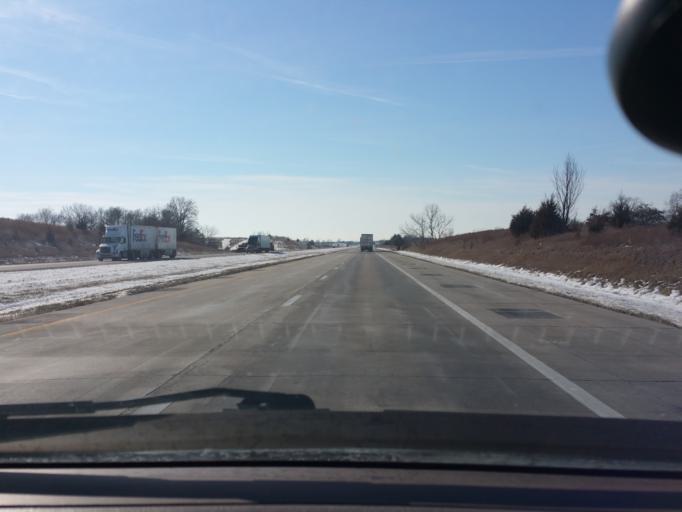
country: US
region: Missouri
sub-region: Harrison County
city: Bethany
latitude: 40.1697
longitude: -94.0225
